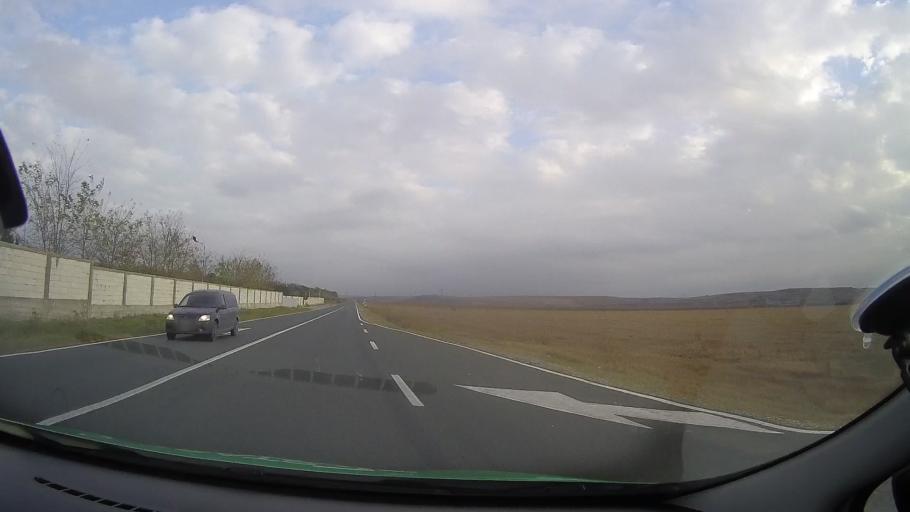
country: RO
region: Constanta
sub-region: Comuna Mircea Voda
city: Mircea Voda
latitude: 44.2709
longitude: 28.1725
